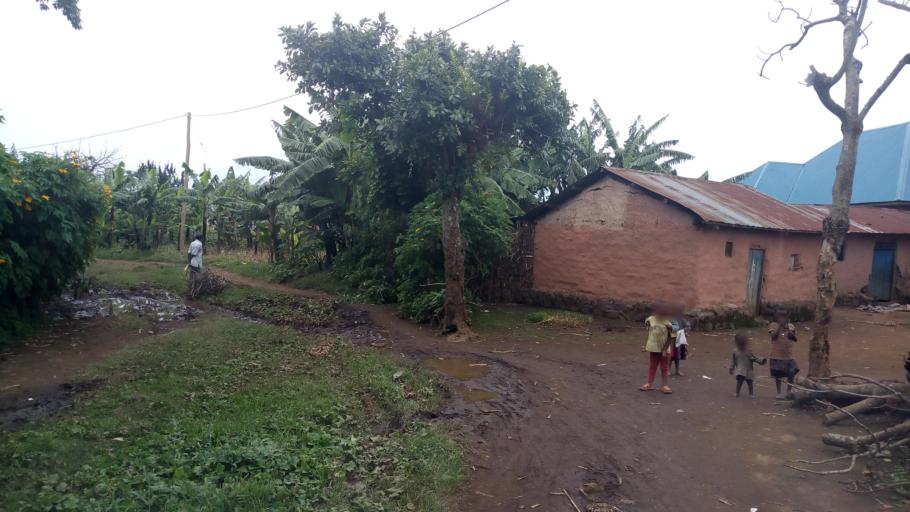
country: UG
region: Western Region
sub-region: Kisoro District
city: Kisoro
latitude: -1.2755
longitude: 29.6232
